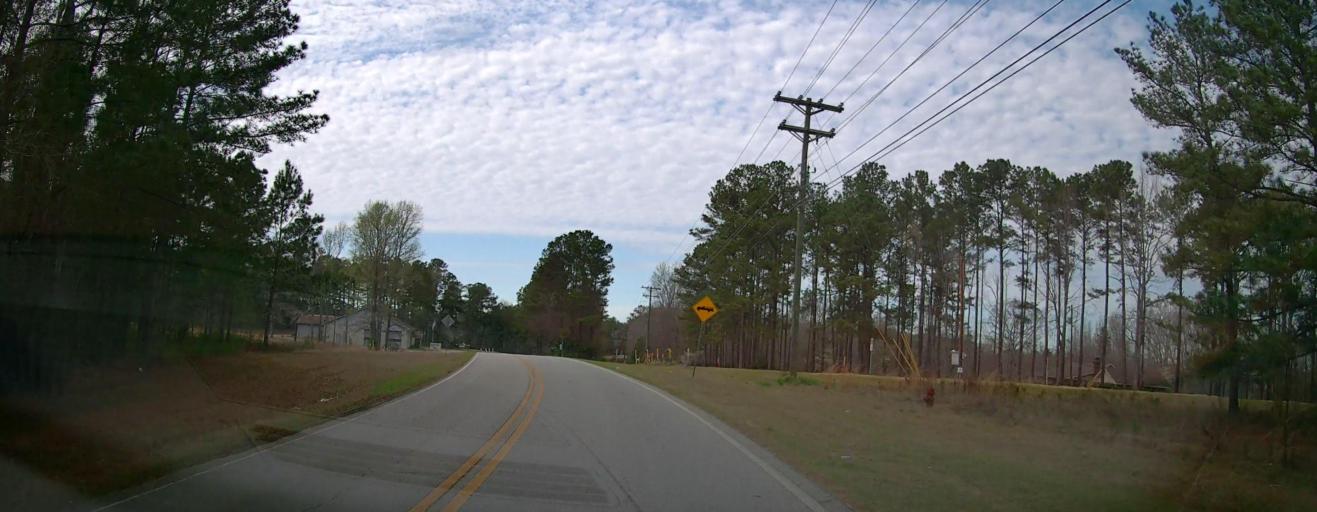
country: US
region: Georgia
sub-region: Bibb County
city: Macon
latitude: 32.9454
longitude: -83.6456
